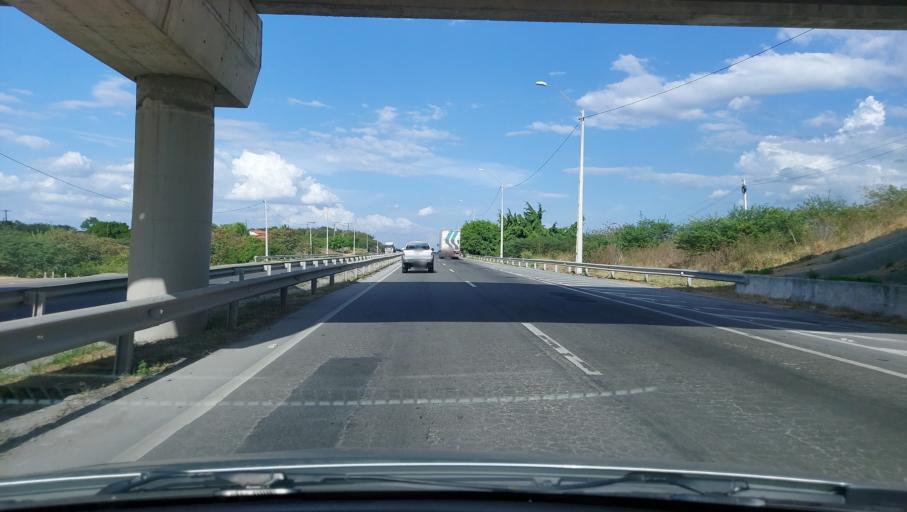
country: BR
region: Bahia
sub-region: Santo Estevao
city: Santo Estevao
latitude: -12.5020
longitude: -39.3545
